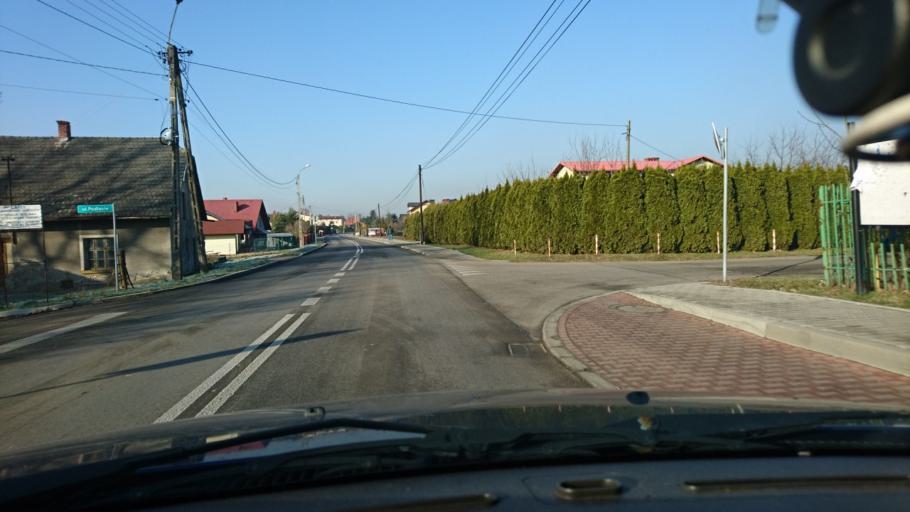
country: PL
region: Silesian Voivodeship
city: Janowice
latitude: 49.8923
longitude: 19.0790
